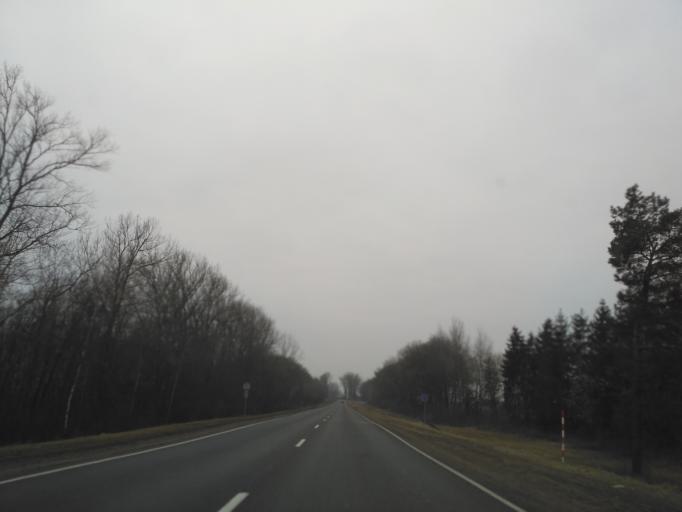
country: BY
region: Brest
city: Baranovichi
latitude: 53.2124
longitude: 26.1311
